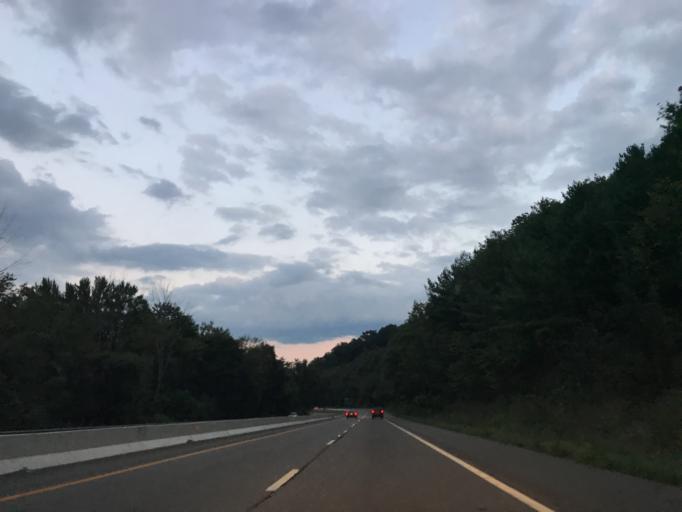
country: US
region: Ohio
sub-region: Columbiana County
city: La Croft
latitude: 40.6379
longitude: -80.5862
